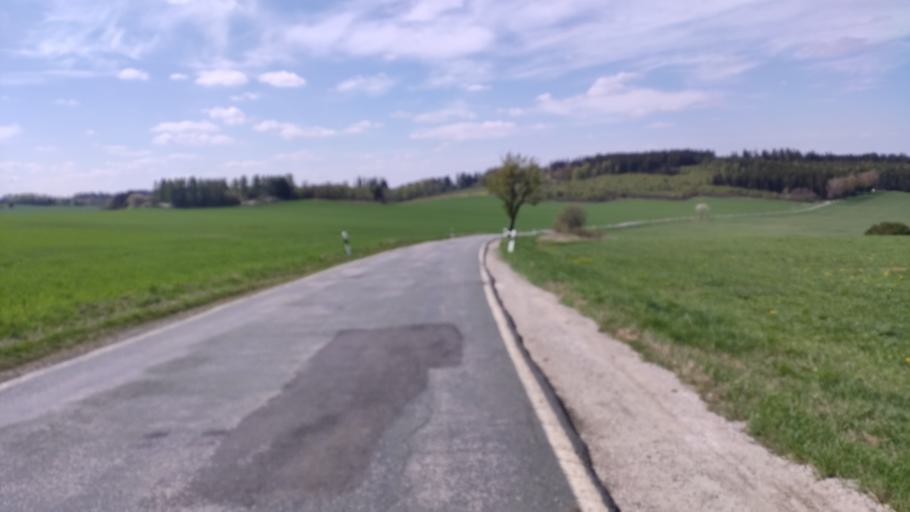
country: DE
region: Thuringia
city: Leutenberg
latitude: 50.4945
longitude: 11.4693
